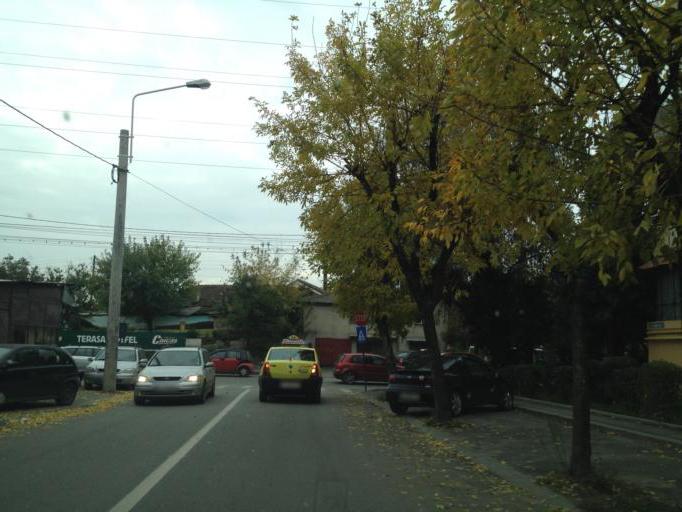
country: RO
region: Dolj
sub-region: Municipiul Craiova
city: Popoveni
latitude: 44.2962
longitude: 23.7976
